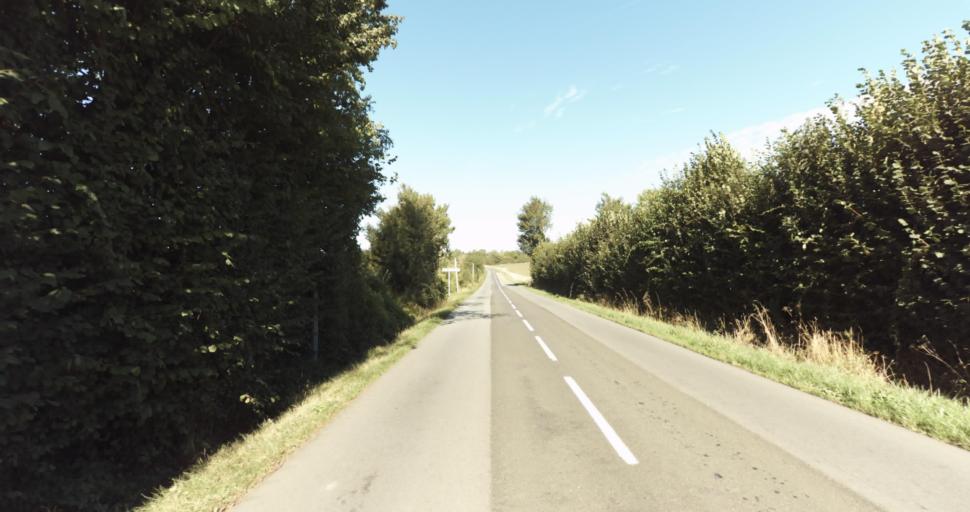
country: FR
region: Lower Normandy
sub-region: Departement de l'Orne
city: Gace
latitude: 48.7918
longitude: 0.2192
